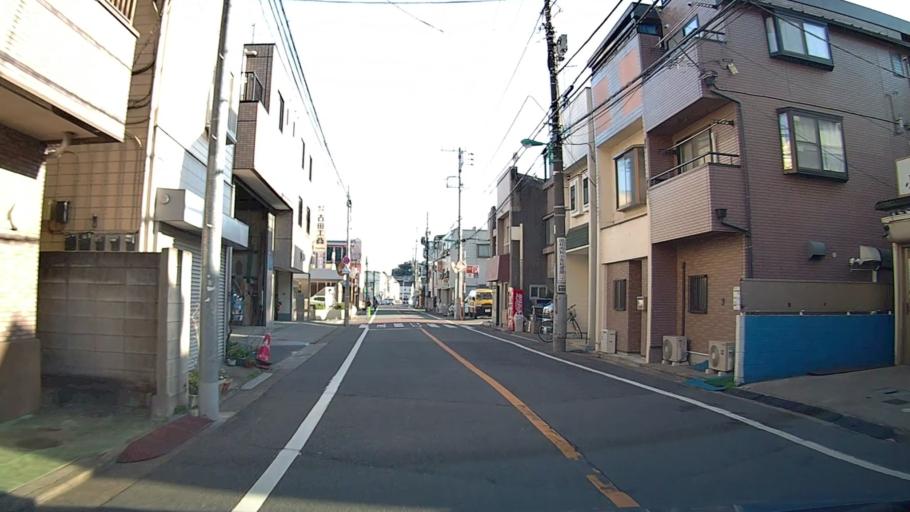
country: JP
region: Saitama
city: Wako
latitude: 35.7550
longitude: 139.6496
